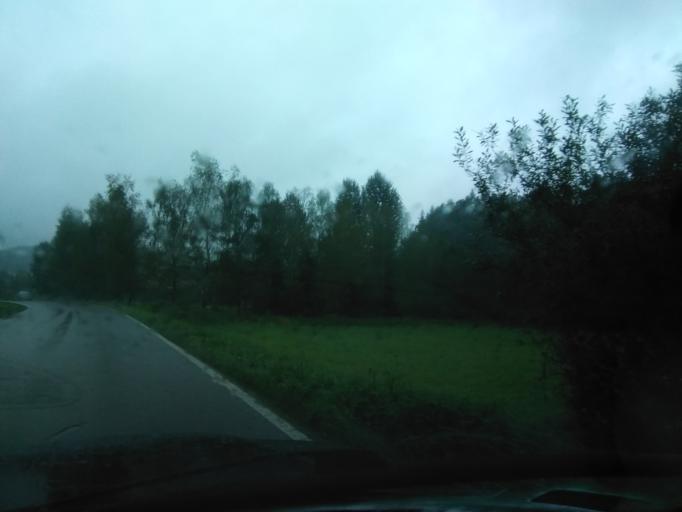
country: PL
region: Subcarpathian Voivodeship
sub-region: Powiat ropczycko-sedziszowski
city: Niedzwiada
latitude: 50.0355
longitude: 21.5447
